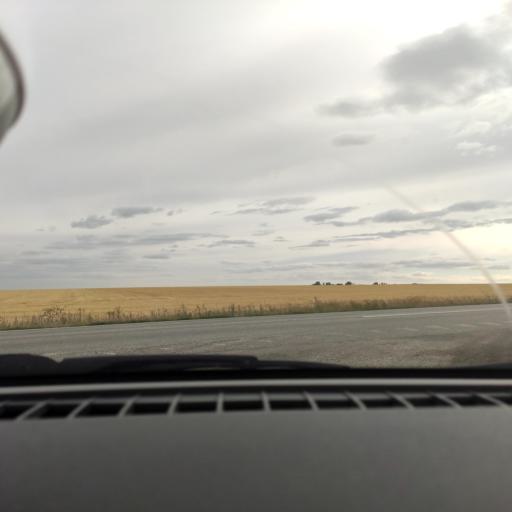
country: RU
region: Samara
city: Georgiyevka
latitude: 53.4178
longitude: 50.9341
